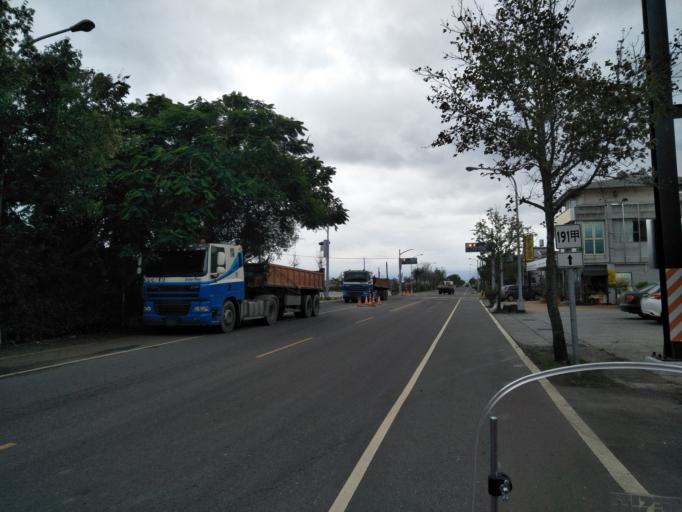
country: TW
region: Taiwan
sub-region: Yilan
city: Yilan
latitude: 24.8175
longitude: 121.7957
